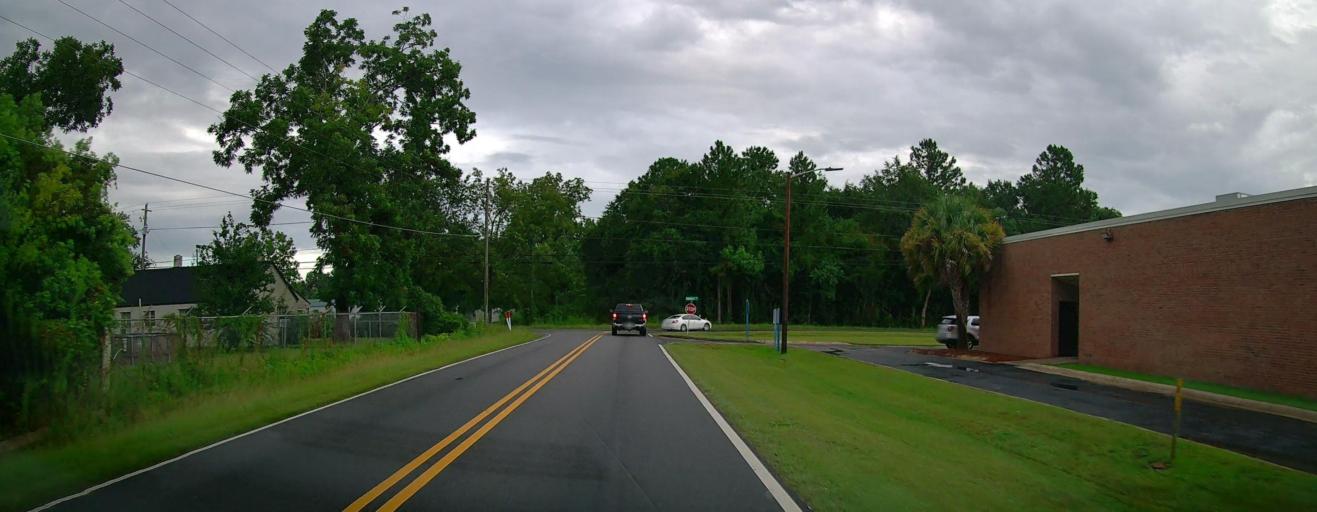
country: US
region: Georgia
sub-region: Ware County
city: Deenwood
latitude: 31.2131
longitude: -82.3836
